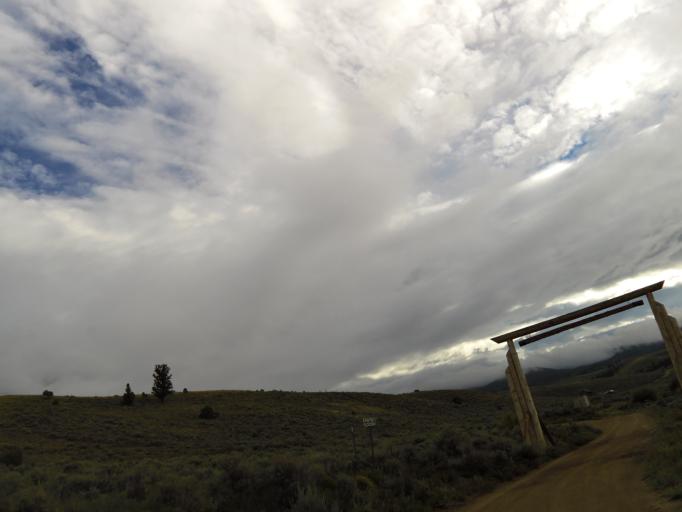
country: US
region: Colorado
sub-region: Chaffee County
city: Salida
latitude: 38.4080
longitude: -106.0627
